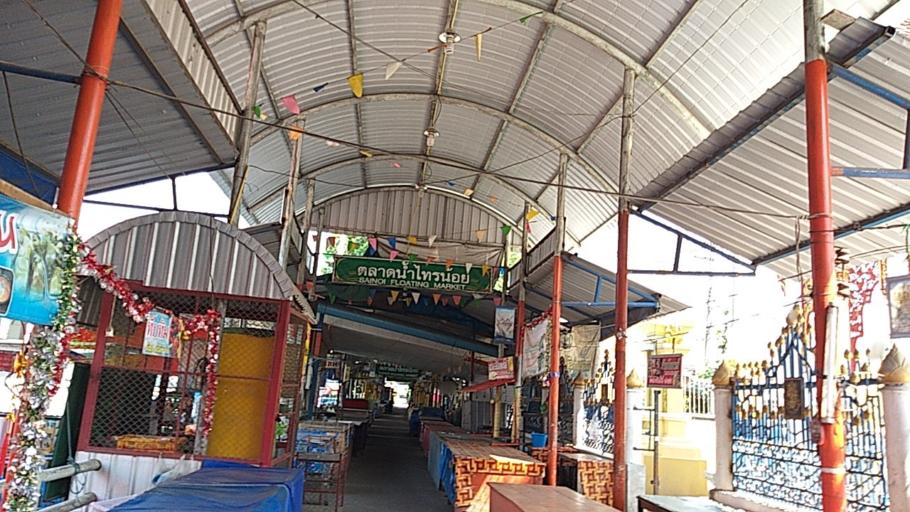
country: TH
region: Nonthaburi
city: Sai Noi
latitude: 13.9788
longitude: 100.3112
